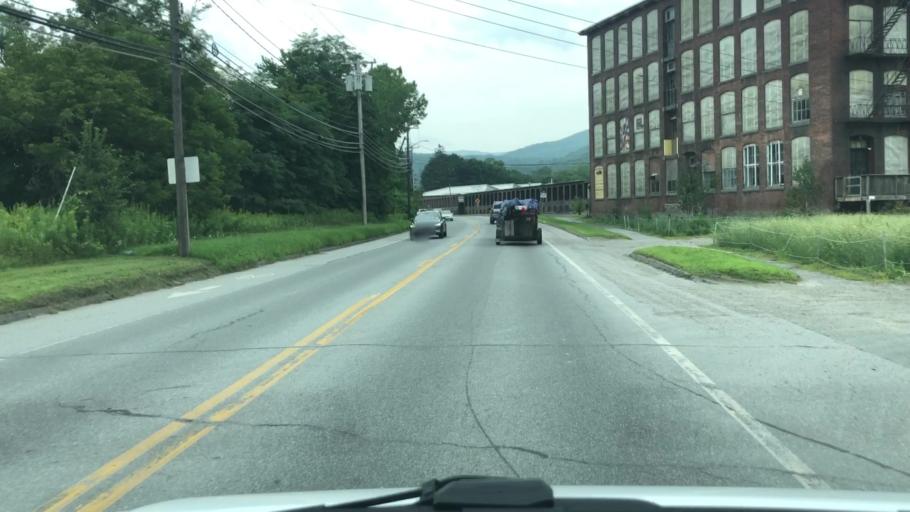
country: US
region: Massachusetts
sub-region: Berkshire County
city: North Adams
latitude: 42.6992
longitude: -73.1535
